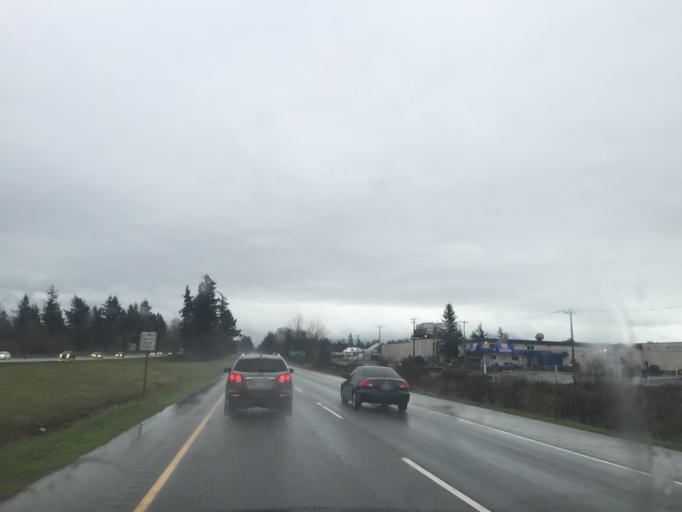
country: CA
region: British Columbia
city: Aldergrove
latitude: 49.0502
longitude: -122.3641
